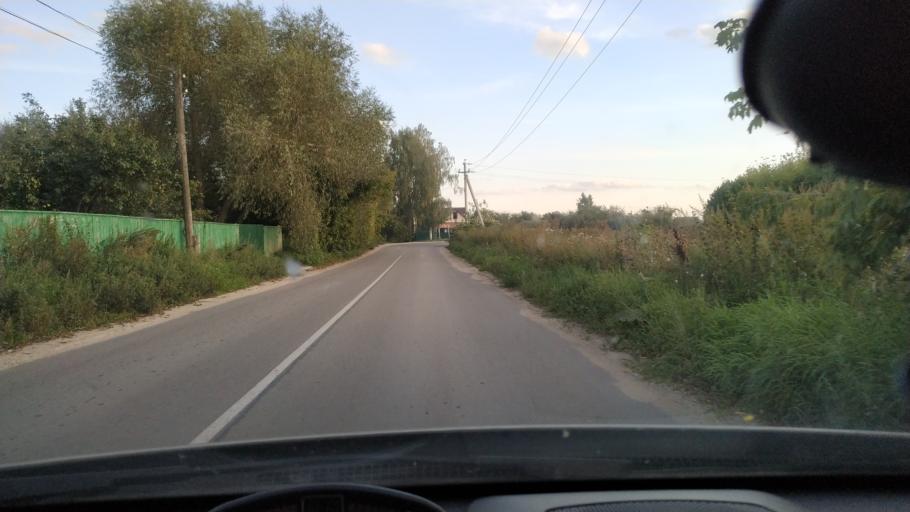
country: RU
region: Rjazan
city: Rybnoye
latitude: 54.8656
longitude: 39.6500
